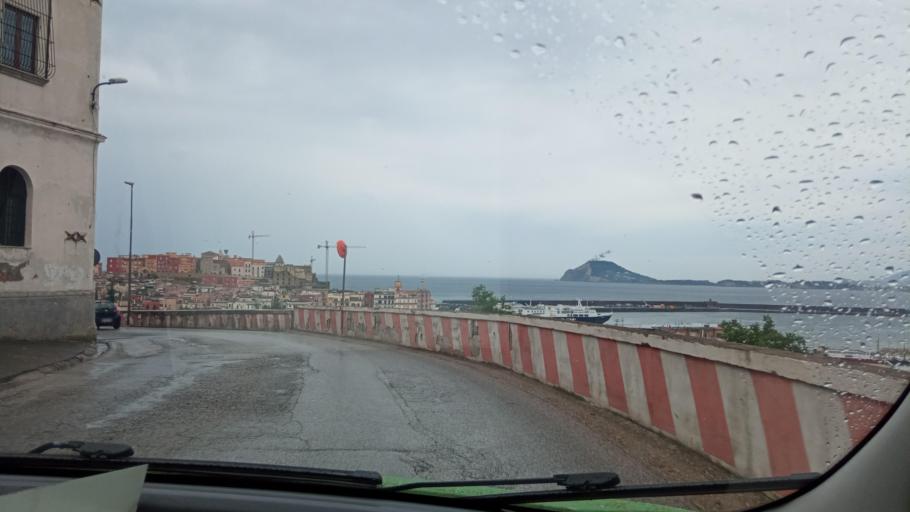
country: IT
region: Campania
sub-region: Provincia di Napoli
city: Pozzuoli
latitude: 40.8285
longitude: 14.1203
